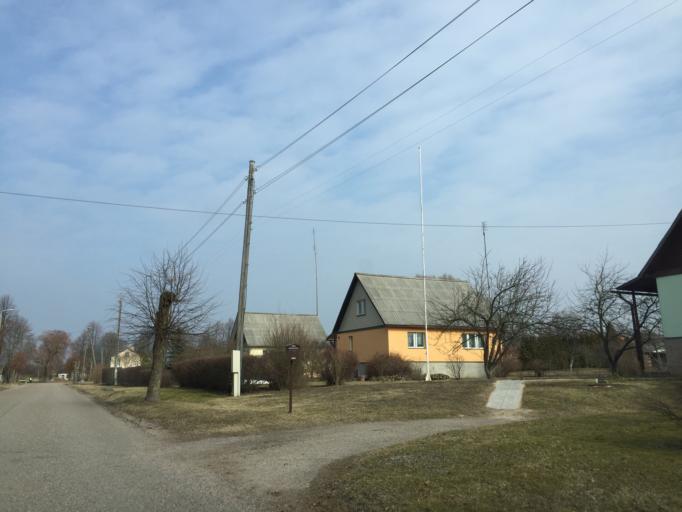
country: LV
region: Salacgrivas
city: Ainazi
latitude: 57.8724
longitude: 24.3608
